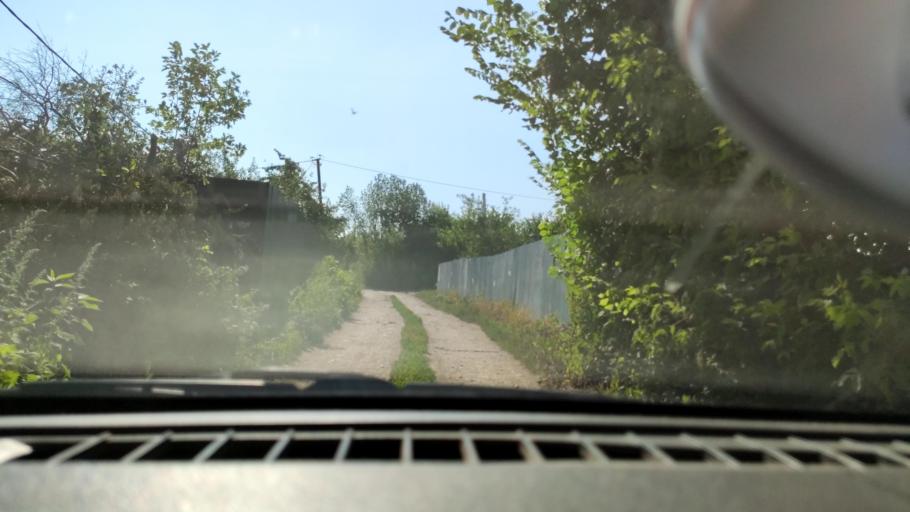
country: RU
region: Samara
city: Petra-Dubrava
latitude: 53.2685
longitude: 50.2896
